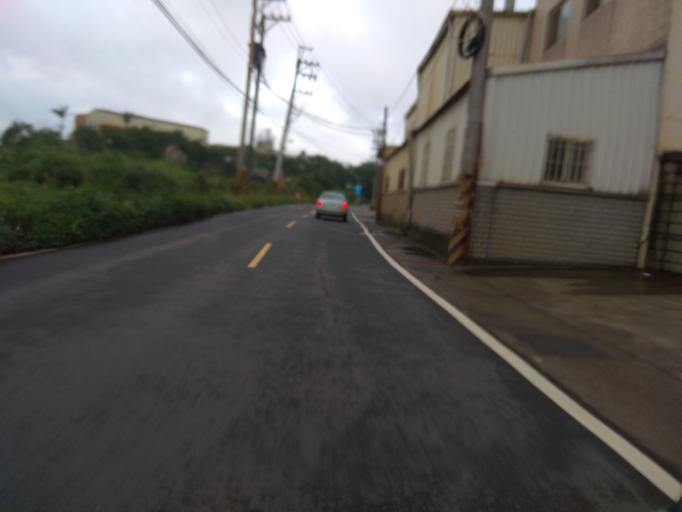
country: TW
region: Taiwan
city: Daxi
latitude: 24.9235
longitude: 121.1511
